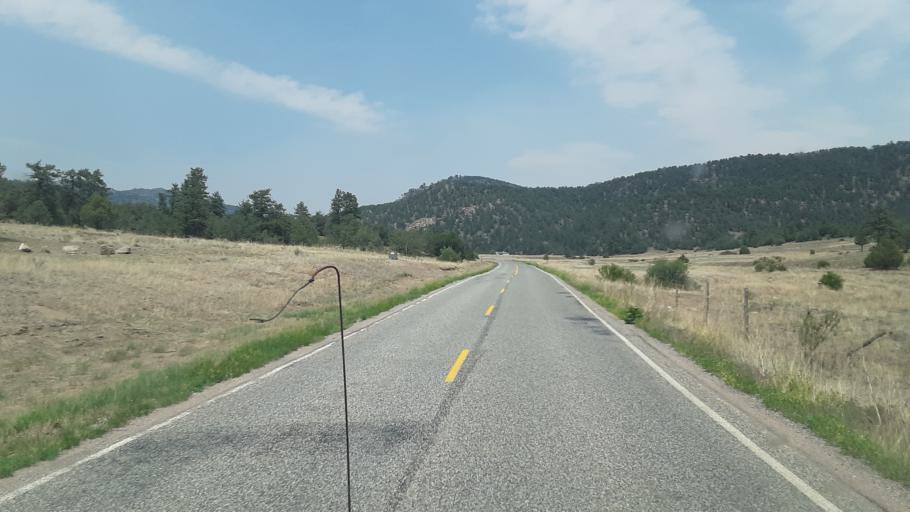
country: US
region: Colorado
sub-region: Fremont County
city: Canon City
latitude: 38.3704
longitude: -105.4588
